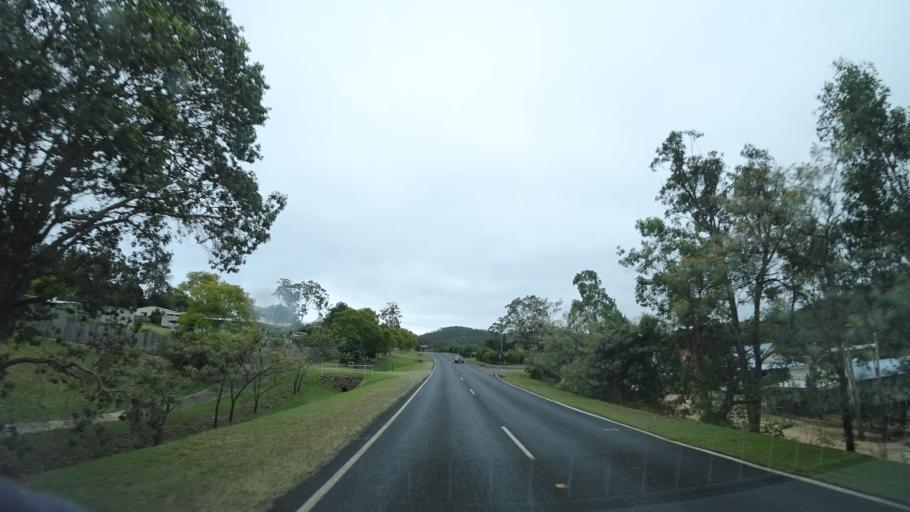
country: AU
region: Queensland
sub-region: Tablelands
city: Atherton
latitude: -17.3753
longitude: 145.3841
